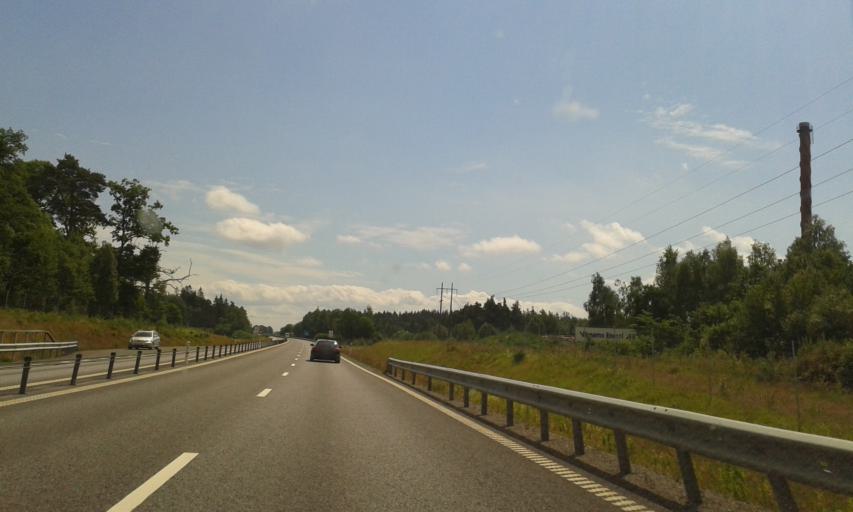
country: SE
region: Joenkoeping
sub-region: Varnamo Kommun
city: Varnamo
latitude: 57.1741
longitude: 14.0085
